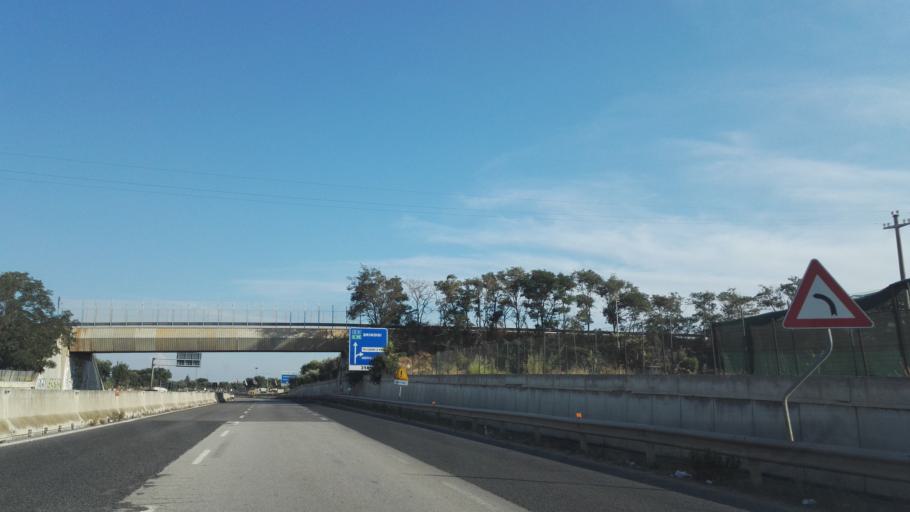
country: IT
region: Apulia
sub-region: Provincia di Bari
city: Polignano a Mare
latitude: 40.9917
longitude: 17.2070
